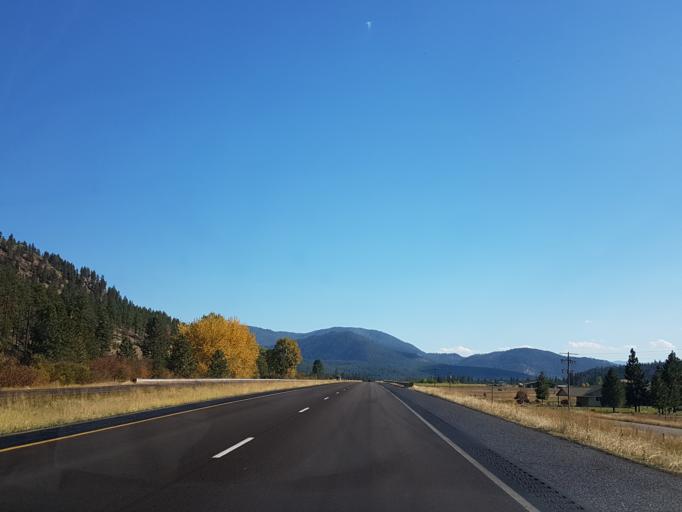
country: US
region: Montana
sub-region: Mineral County
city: Superior
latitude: 47.1434
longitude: -114.8151
